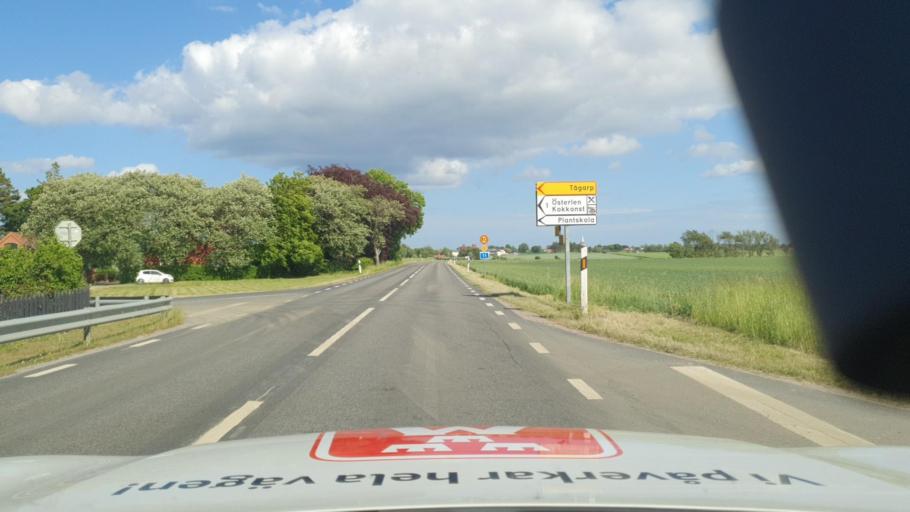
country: SE
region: Skane
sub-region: Simrishamns Kommun
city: Simrishamn
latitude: 55.5385
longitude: 14.2155
